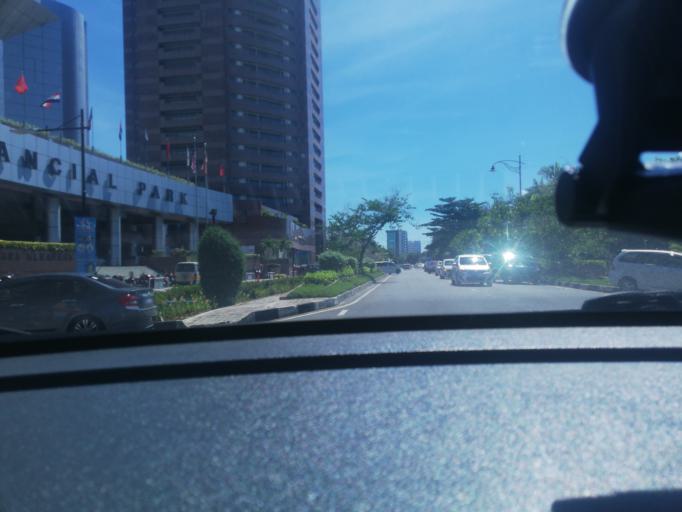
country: MY
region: Labuan
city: Victoria
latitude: 5.2769
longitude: 115.2497
